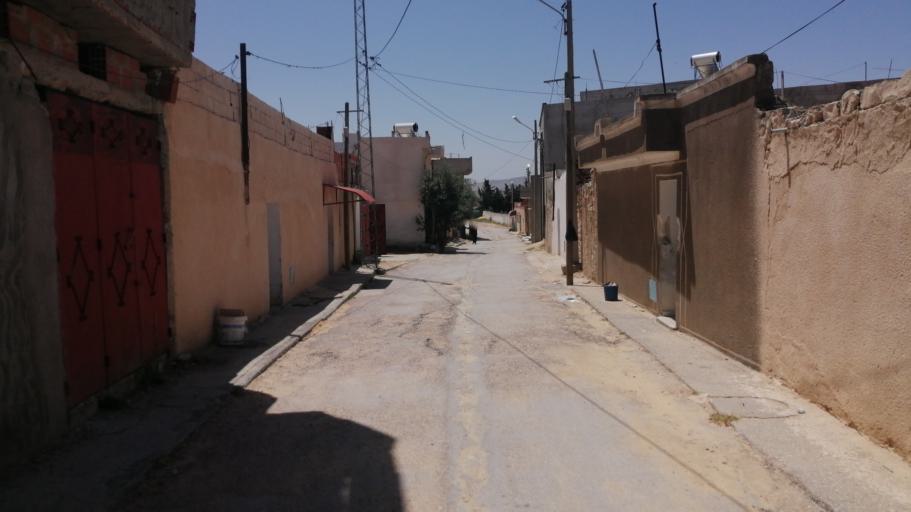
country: TN
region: Silyanah
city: Maktar
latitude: 35.8501
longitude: 9.2040
